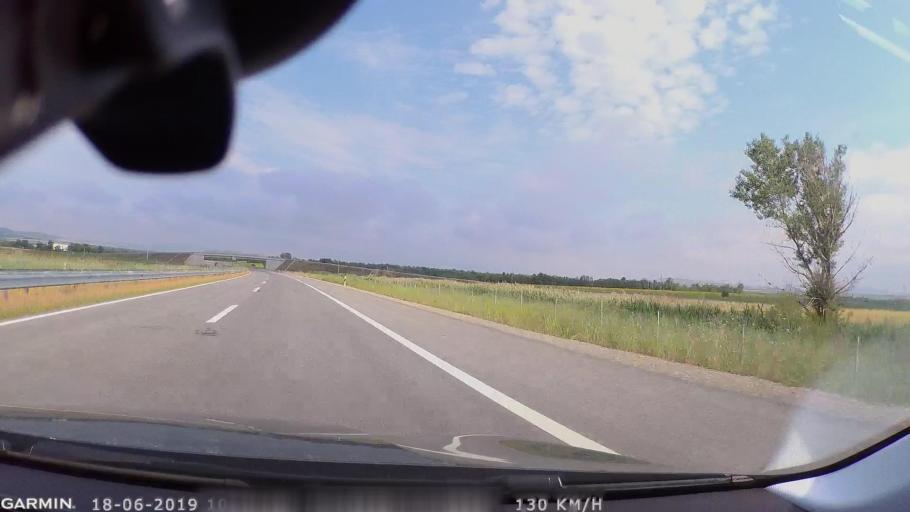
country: MK
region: Sveti Nikole
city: Sveti Nikole
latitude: 41.8261
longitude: 22.0079
